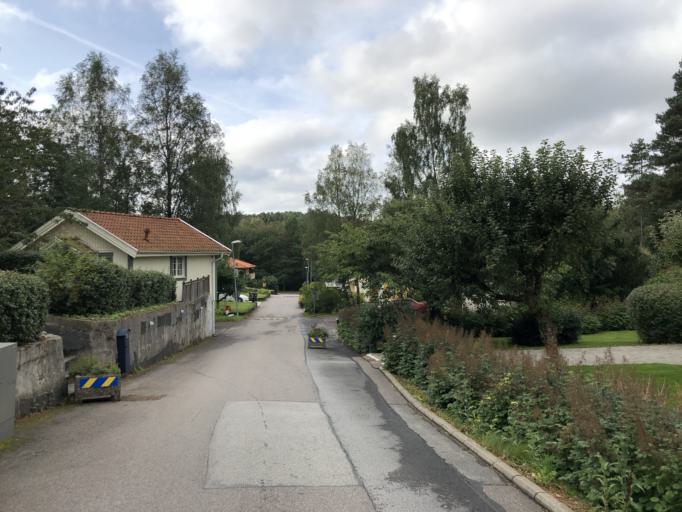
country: SE
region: Vaestra Goetaland
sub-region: Goteborg
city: Majorna
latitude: 57.7418
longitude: 11.9045
